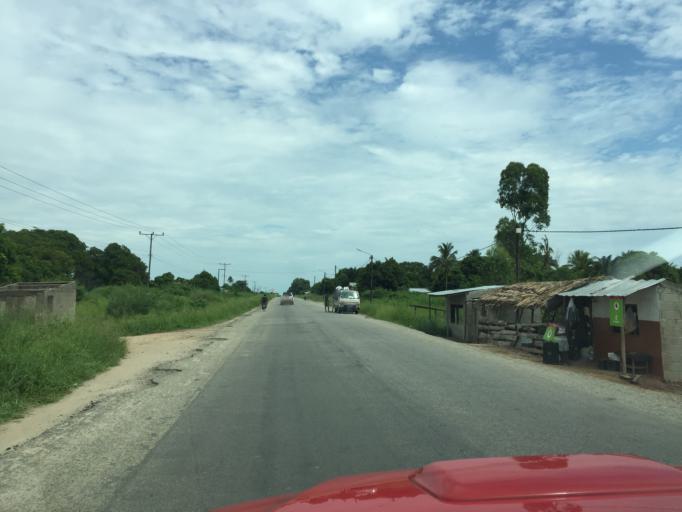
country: MZ
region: Zambezia
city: Quelimane
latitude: -17.5865
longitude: 36.8102
